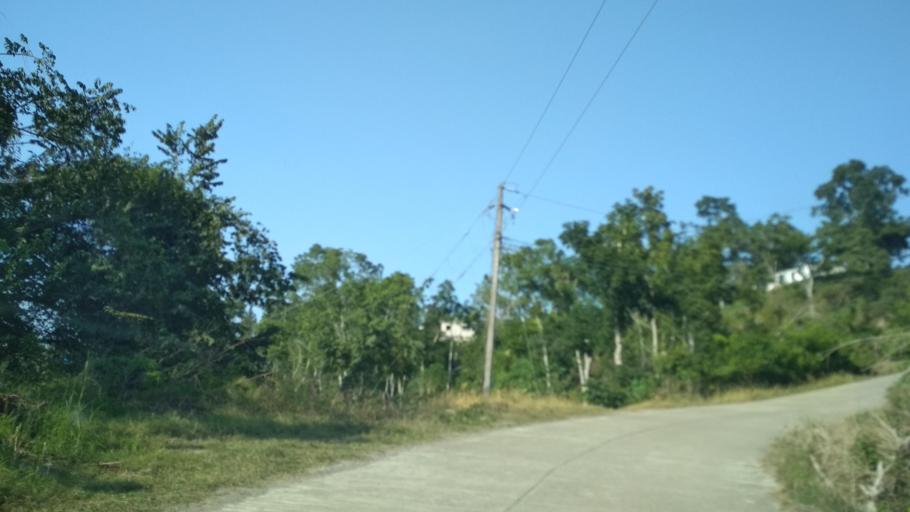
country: MX
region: Puebla
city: San Jose Acateno
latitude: 20.2145
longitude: -97.2645
